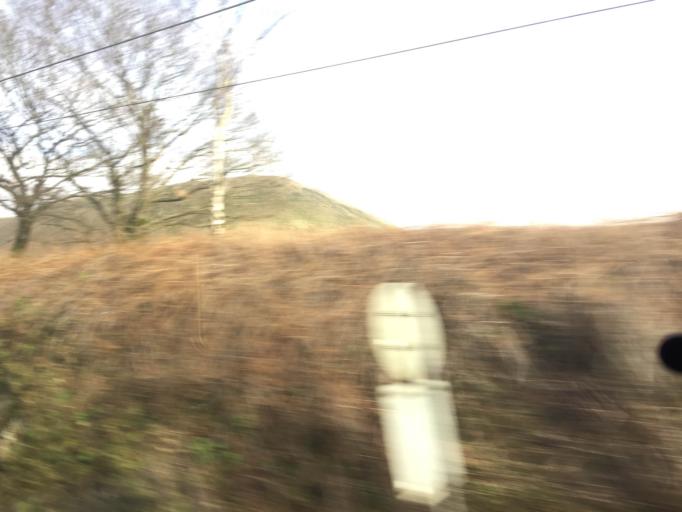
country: GB
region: England
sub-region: Cumbria
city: Sedbergh
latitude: 54.3860
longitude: -2.5842
